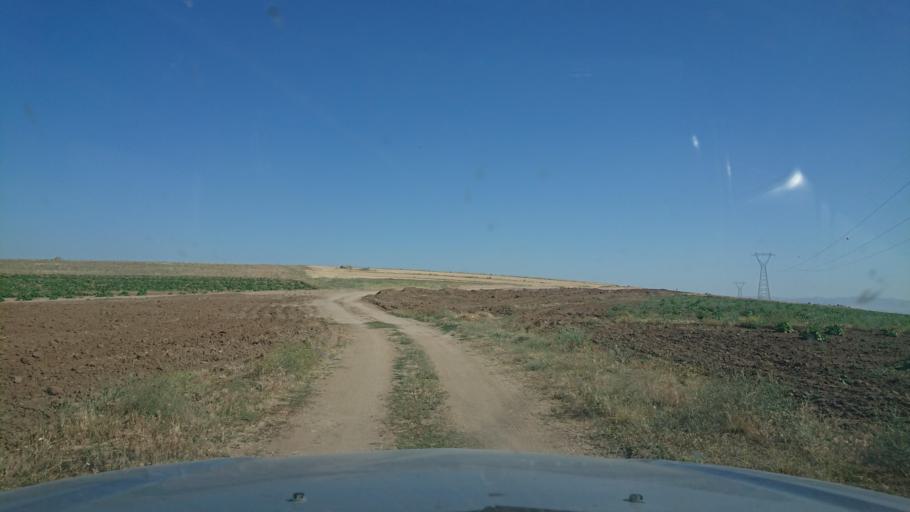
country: TR
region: Aksaray
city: Agacoren
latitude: 38.8367
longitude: 33.9448
